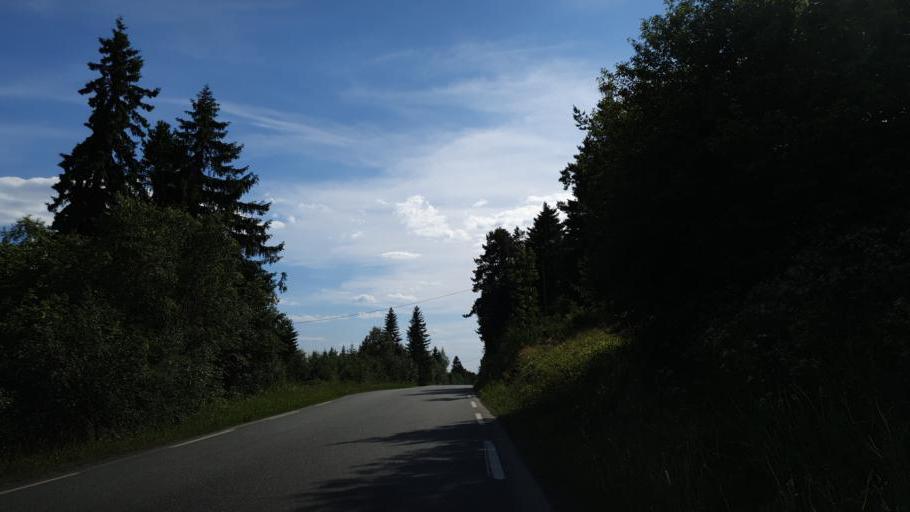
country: NO
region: Nord-Trondelag
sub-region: Leksvik
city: Leksvik
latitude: 63.6344
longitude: 10.5731
